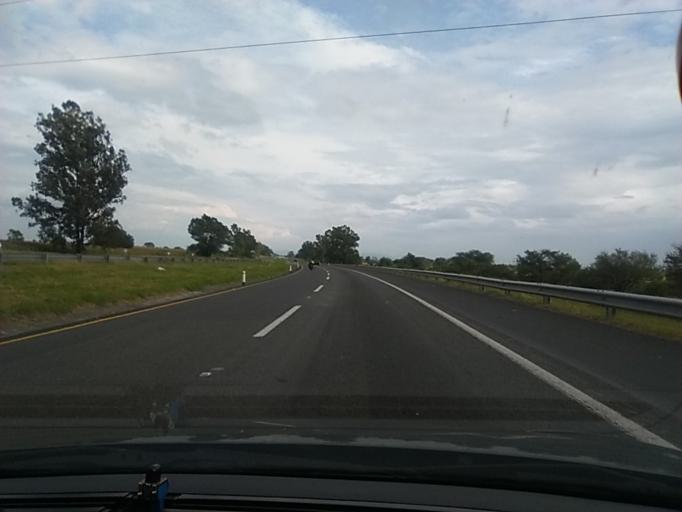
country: MX
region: Jalisco
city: Jamay
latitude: 20.3494
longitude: -102.6317
